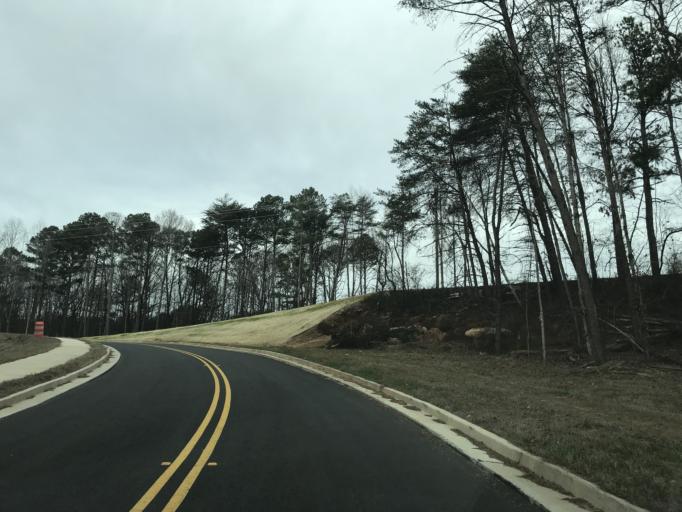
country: US
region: Georgia
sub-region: Forsyth County
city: Cumming
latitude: 34.2287
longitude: -84.0987
